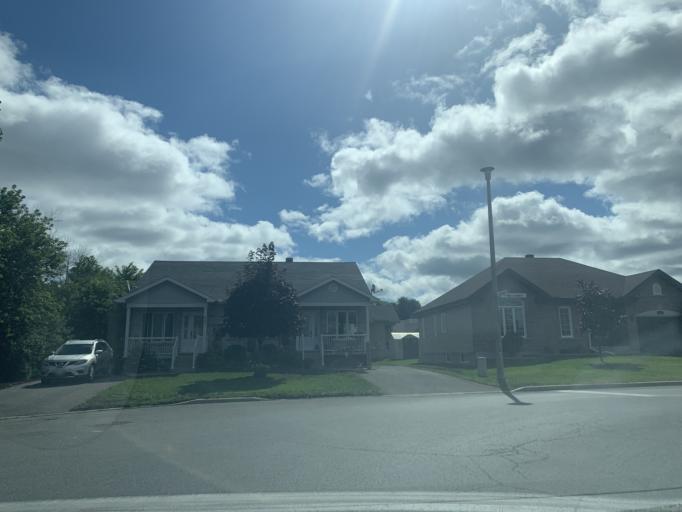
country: CA
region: Ontario
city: Hawkesbury
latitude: 45.6041
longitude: -74.5809
